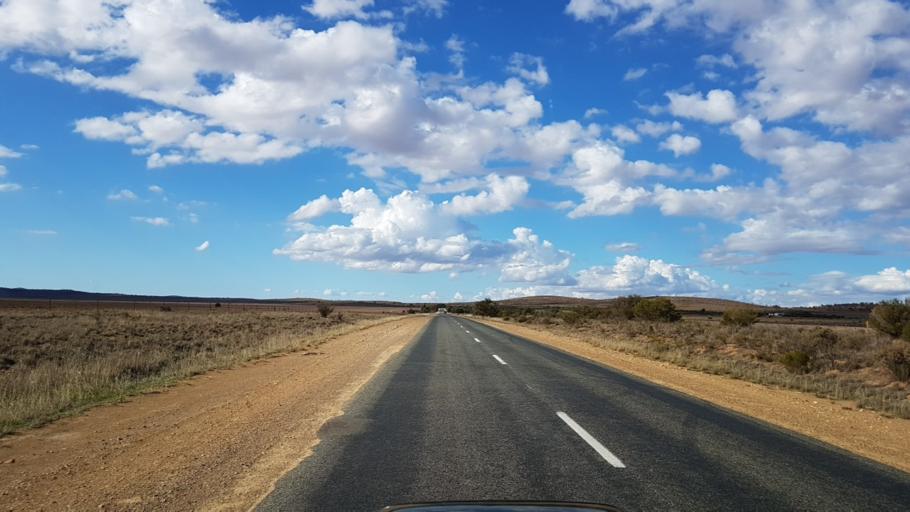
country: AU
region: South Australia
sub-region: Peterborough
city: Peterborough
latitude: -32.9657
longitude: 138.8767
